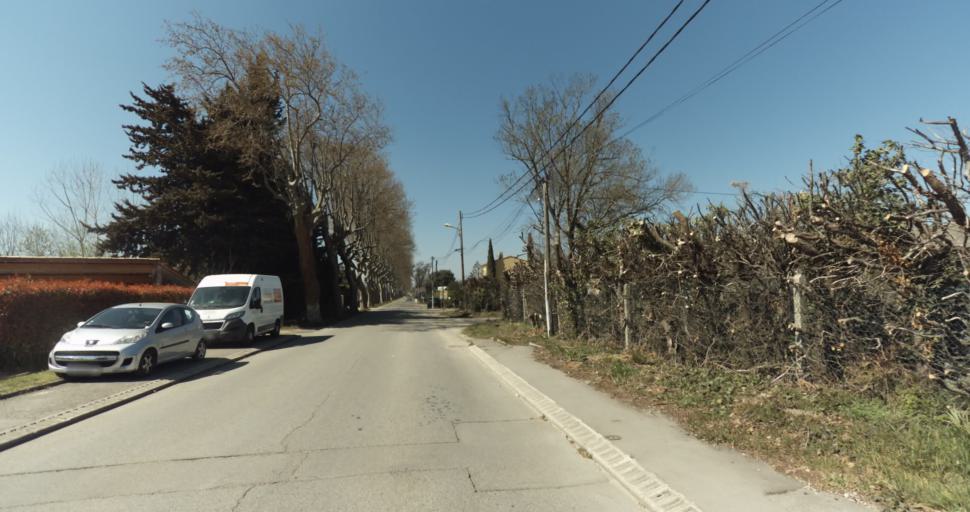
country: FR
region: Provence-Alpes-Cote d'Azur
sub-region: Departement des Bouches-du-Rhone
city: Pelissanne
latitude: 43.6276
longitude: 5.1651
